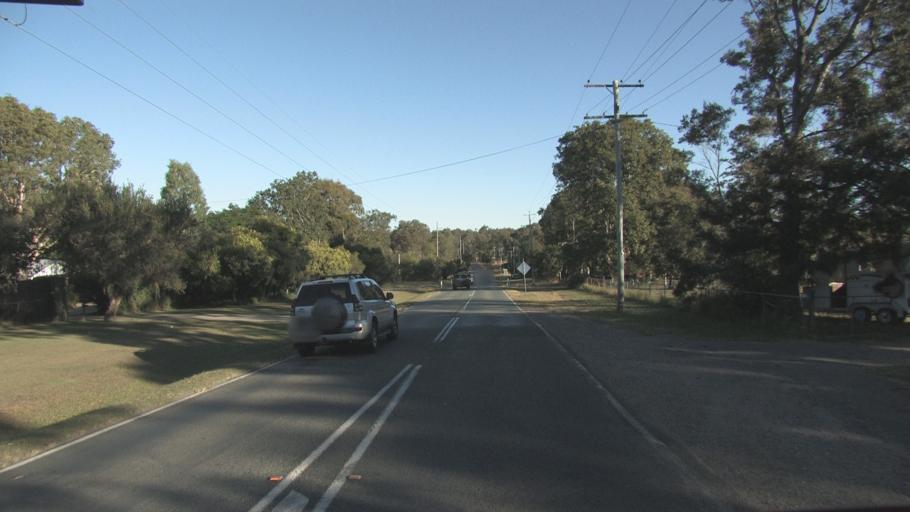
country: AU
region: Queensland
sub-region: Logan
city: Logan Reserve
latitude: -27.7362
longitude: 153.0879
